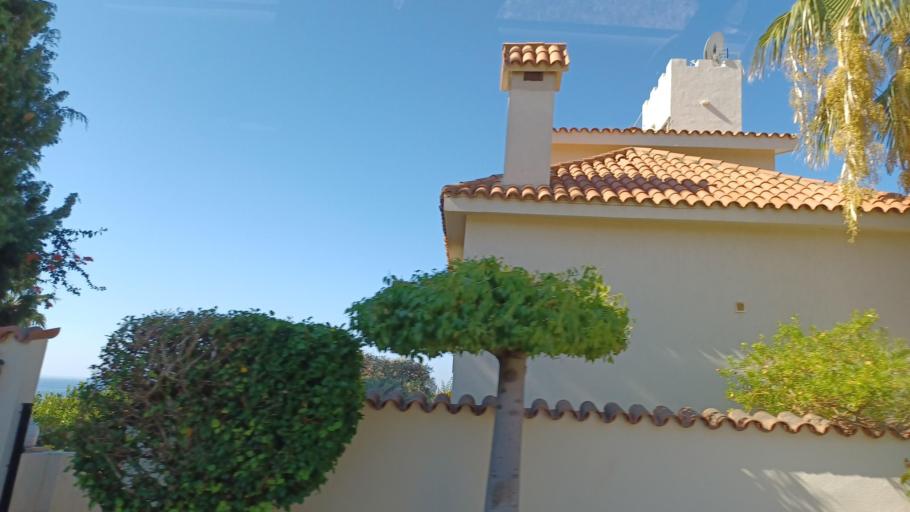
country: CY
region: Pafos
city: Pegeia
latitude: 34.8562
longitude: 32.3695
